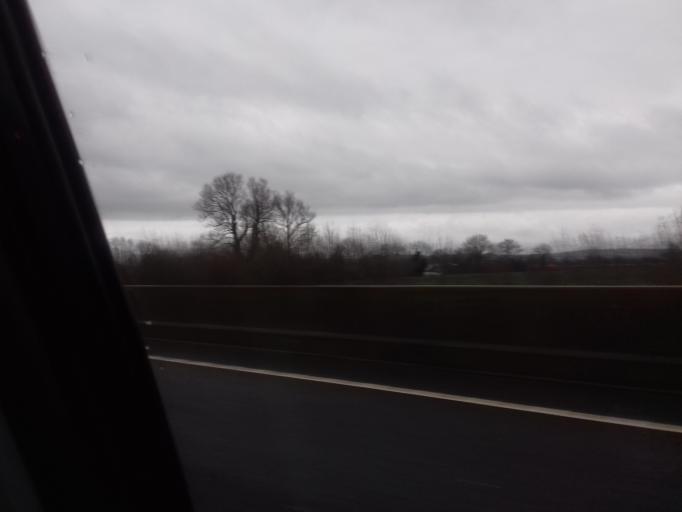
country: IE
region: Leinster
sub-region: County Carlow
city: Bagenalstown
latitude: 52.7149
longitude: -7.0127
